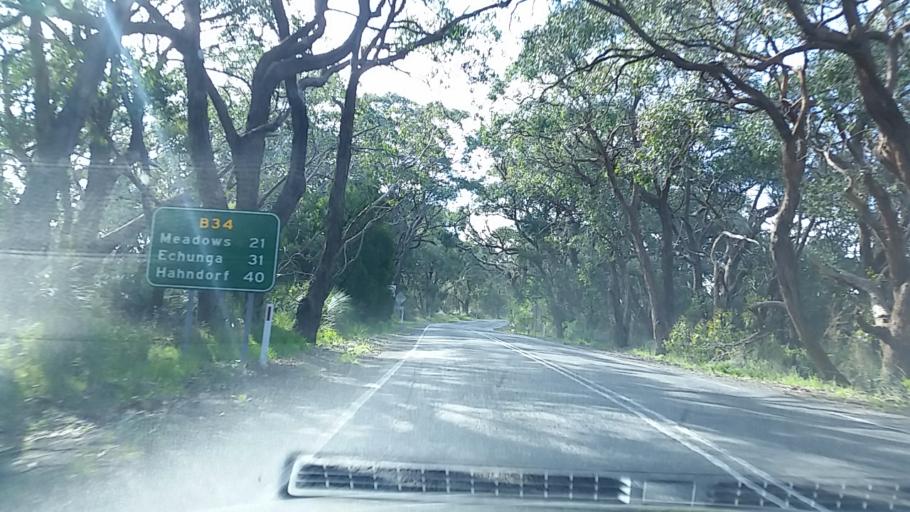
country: AU
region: South Australia
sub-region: Alexandrina
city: Mount Compass
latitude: -35.2957
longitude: 138.5821
